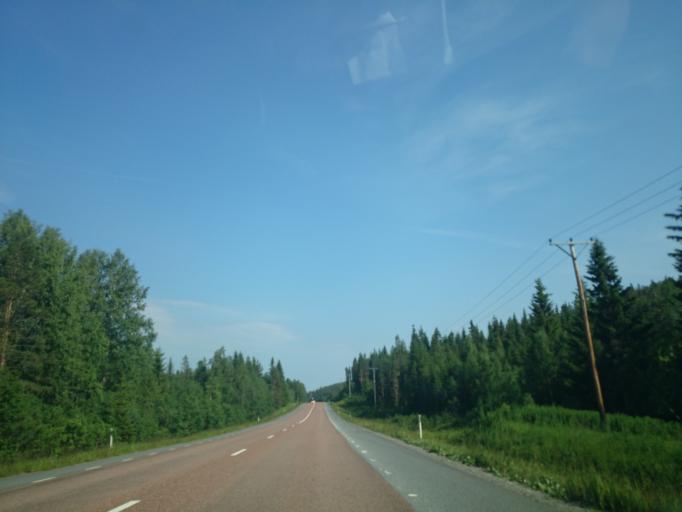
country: SE
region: Jaemtland
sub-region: Braecke Kommun
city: Braecke
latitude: 62.9418
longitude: 15.1834
